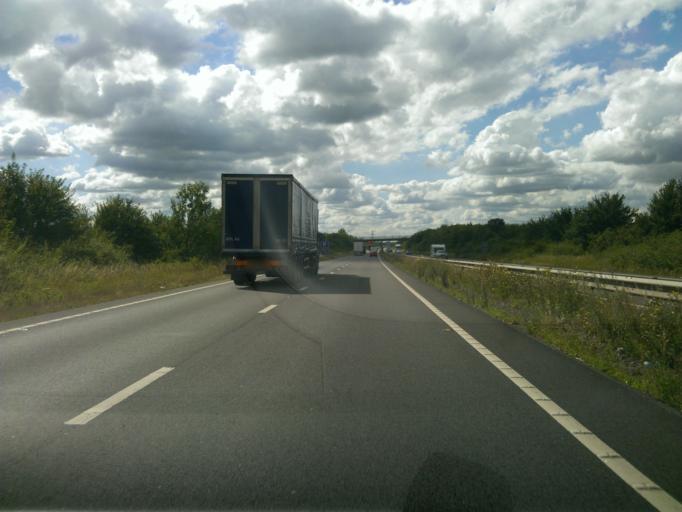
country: GB
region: England
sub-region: Northamptonshire
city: Long Buckby
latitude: 52.3925
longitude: -1.1021
